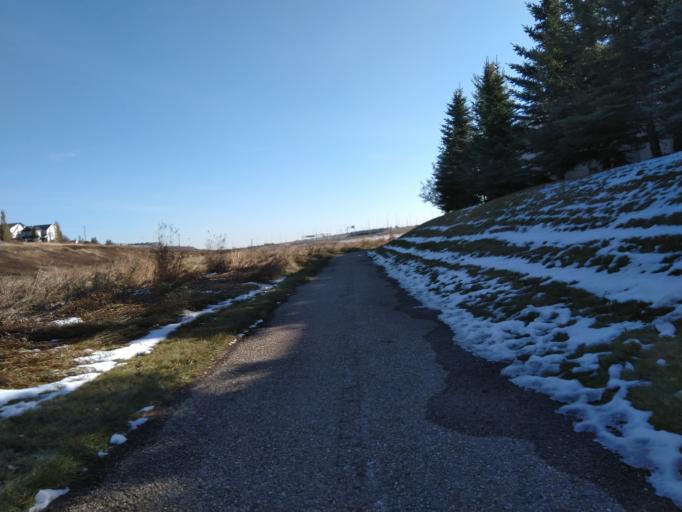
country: CA
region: Alberta
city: Calgary
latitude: 51.1619
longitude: -114.1221
